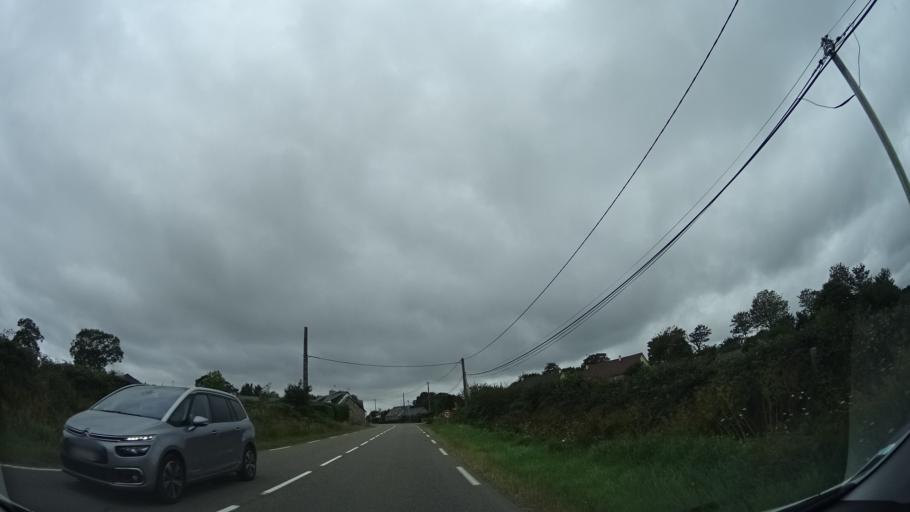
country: FR
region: Lower Normandy
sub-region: Departement de la Manche
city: La Haye-du-Puits
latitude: 49.3056
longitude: -1.5858
